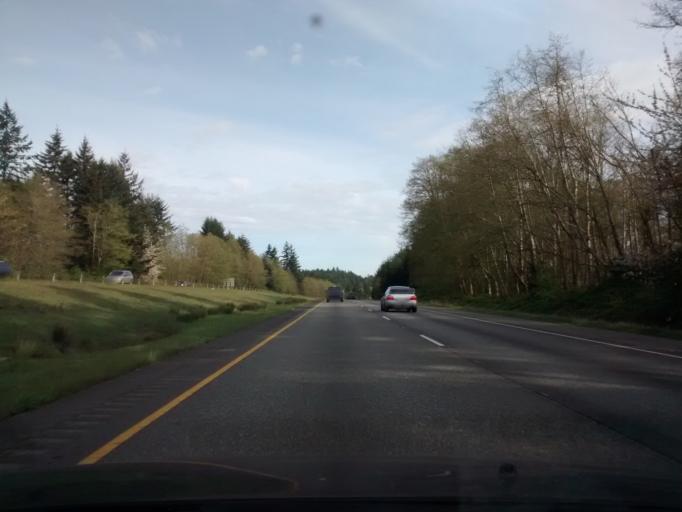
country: US
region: Washington
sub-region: Kitsap County
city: Silverdale
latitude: 47.6464
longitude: -122.7058
